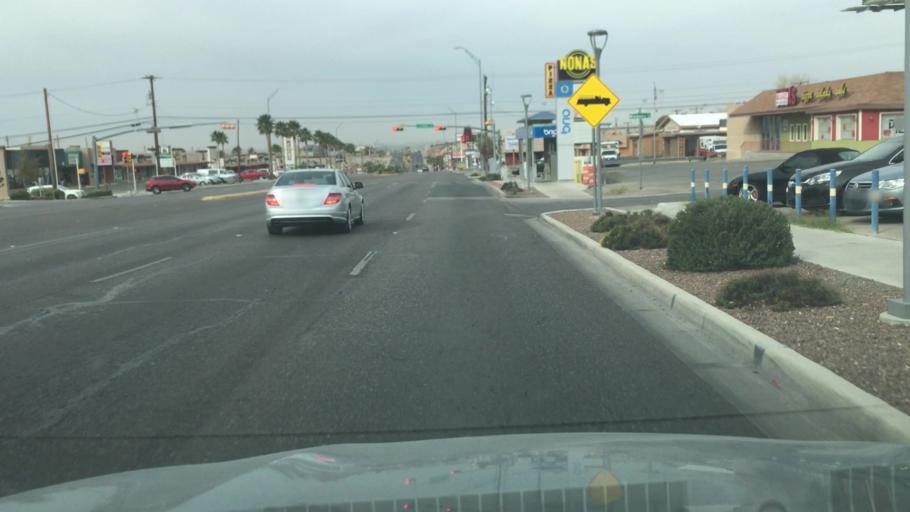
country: US
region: New Mexico
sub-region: Dona Ana County
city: Sunland Park
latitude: 31.8330
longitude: -106.5362
